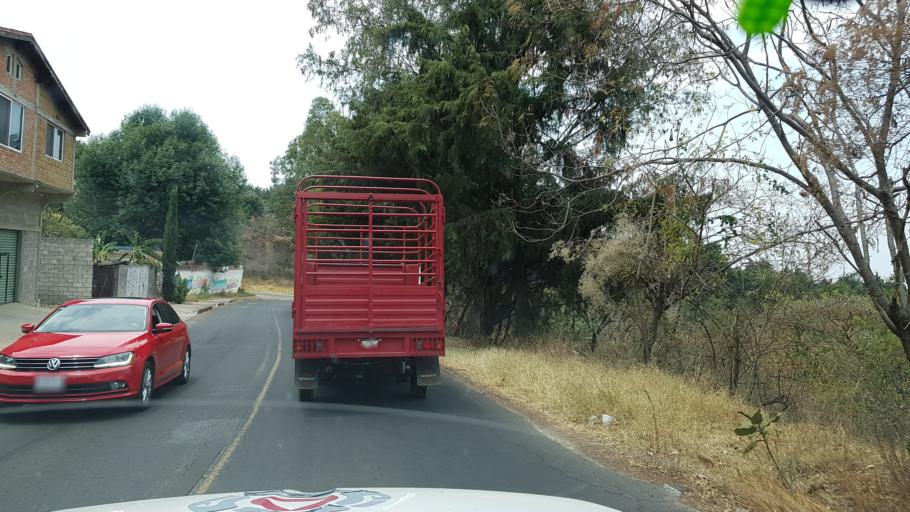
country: MX
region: Morelos
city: Ocuituco
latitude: 18.8789
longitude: -98.7794
